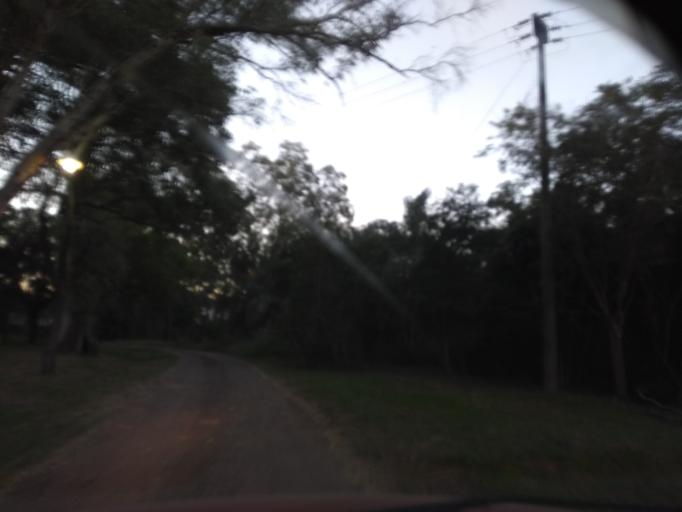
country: AR
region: Chaco
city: Fontana
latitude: -27.4226
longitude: -59.0047
